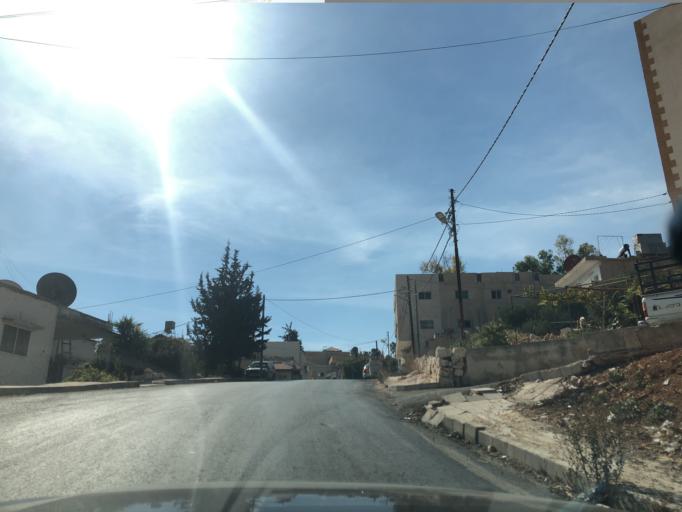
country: JO
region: Ajlun
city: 'Ajlun
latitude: 32.3307
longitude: 35.7415
